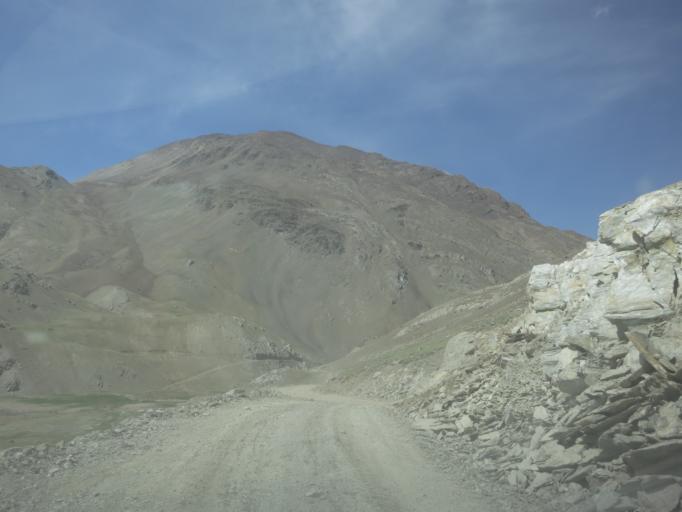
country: IN
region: Himachal Pradesh
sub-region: Kulu
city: Manali
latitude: 32.4171
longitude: 77.6516
